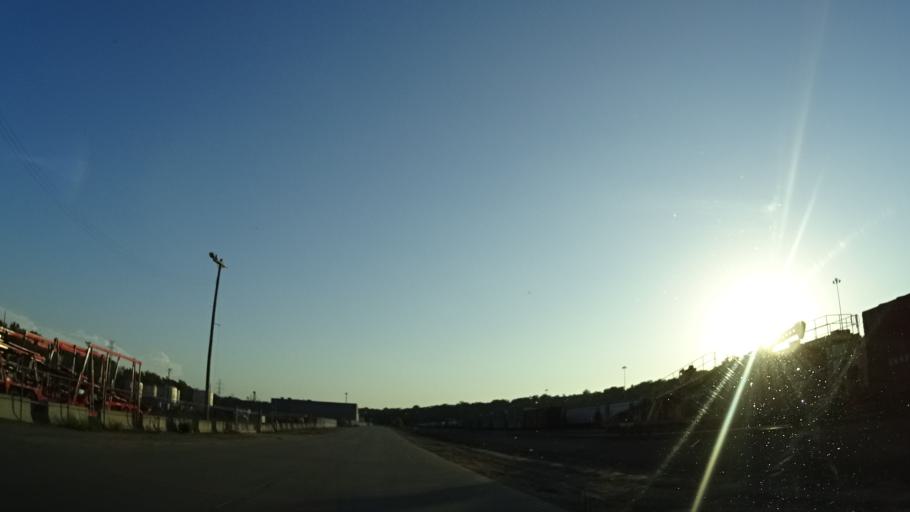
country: US
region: Nebraska
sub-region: Douglas County
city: Omaha
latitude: 41.2232
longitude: -95.9205
